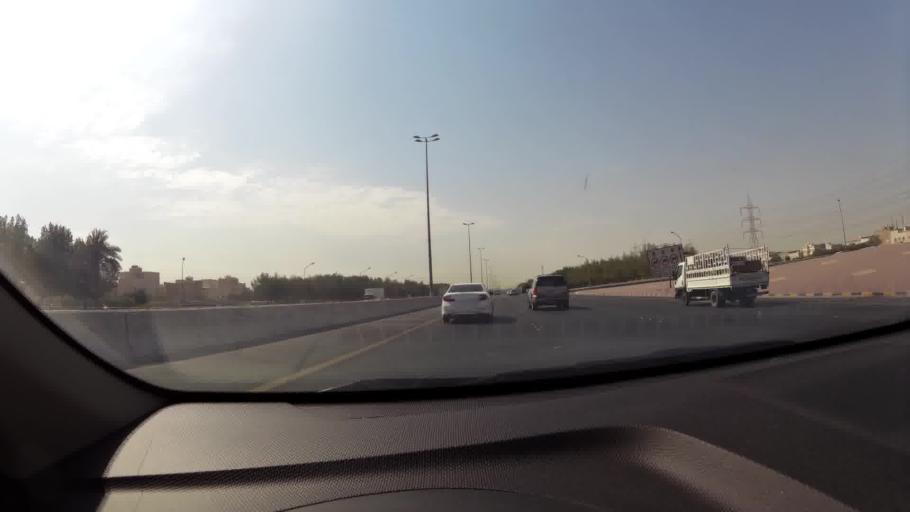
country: KW
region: Mubarak al Kabir
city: Mubarak al Kabir
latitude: 29.1679
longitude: 48.0727
